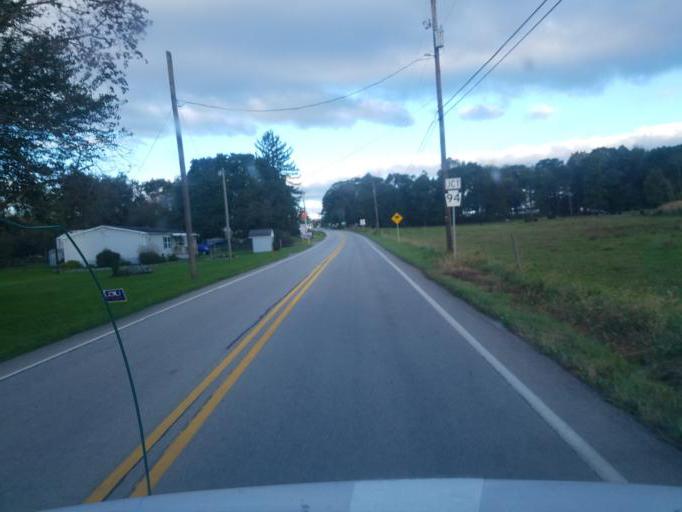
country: US
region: Pennsylvania
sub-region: Adams County
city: Lake Meade
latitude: 39.9380
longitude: -77.0590
